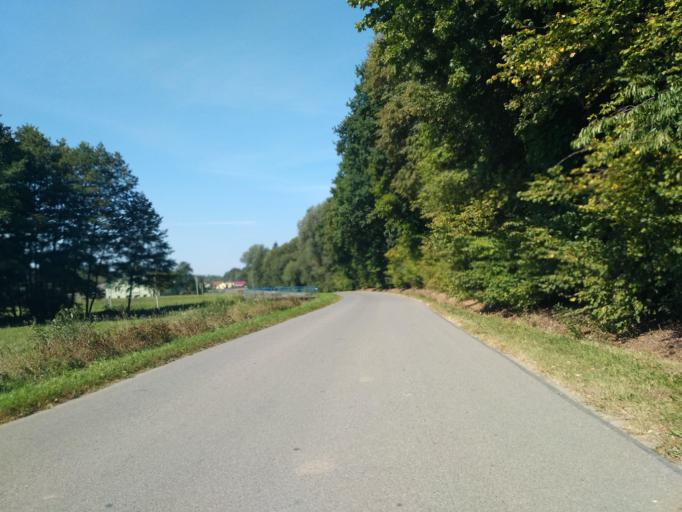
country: PL
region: Subcarpathian Voivodeship
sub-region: Powiat brzozowski
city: Niebocko
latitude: 49.6408
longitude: 22.1140
